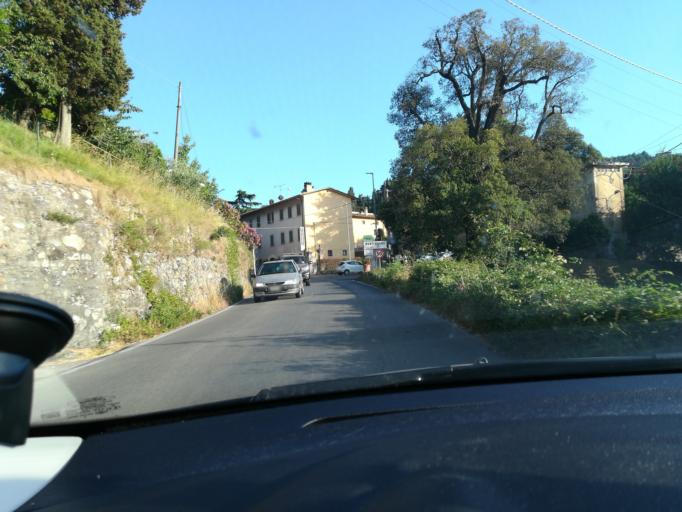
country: IT
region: Tuscany
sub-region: Provincia di Lucca
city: Stiava
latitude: 43.9114
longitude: 10.3387
